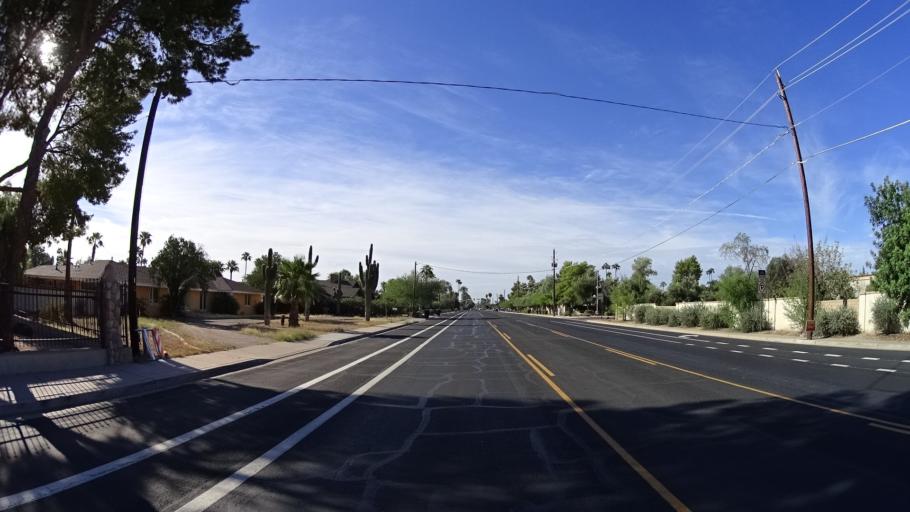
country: US
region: Arizona
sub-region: Maricopa County
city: Paradise Valley
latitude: 33.5043
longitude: -111.9433
